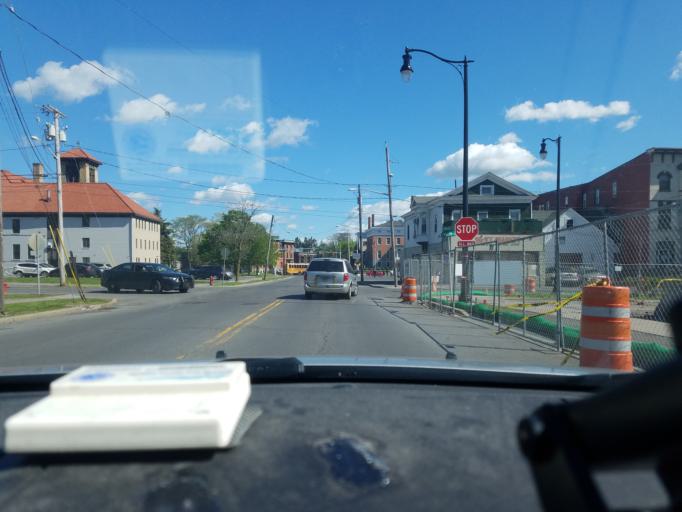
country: US
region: New York
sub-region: Onondaga County
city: Syracuse
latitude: 43.0547
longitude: -76.1469
